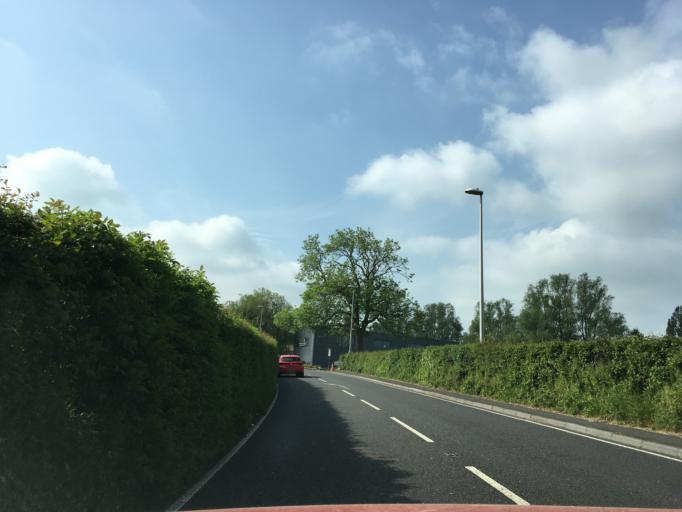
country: GB
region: England
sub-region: North Somerset
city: Nailsea
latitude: 51.4394
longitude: -2.7636
